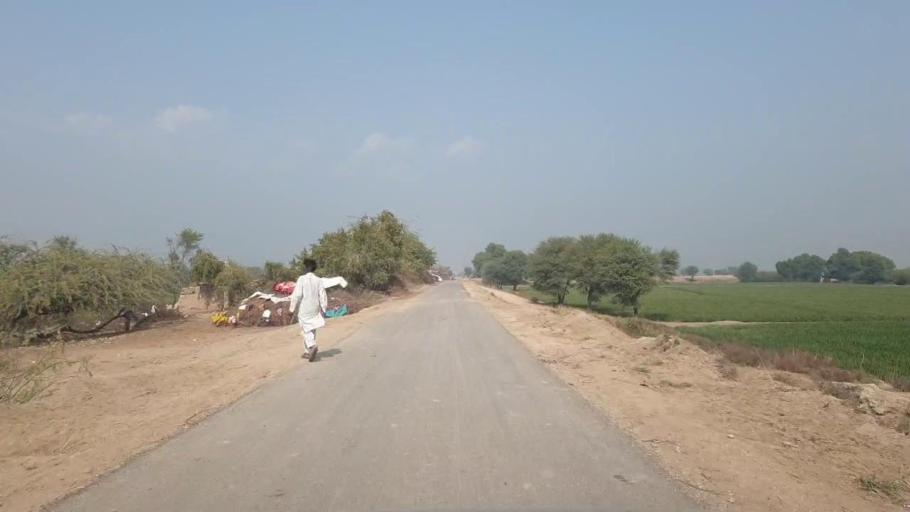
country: PK
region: Sindh
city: Hala
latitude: 25.7829
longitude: 68.3997
